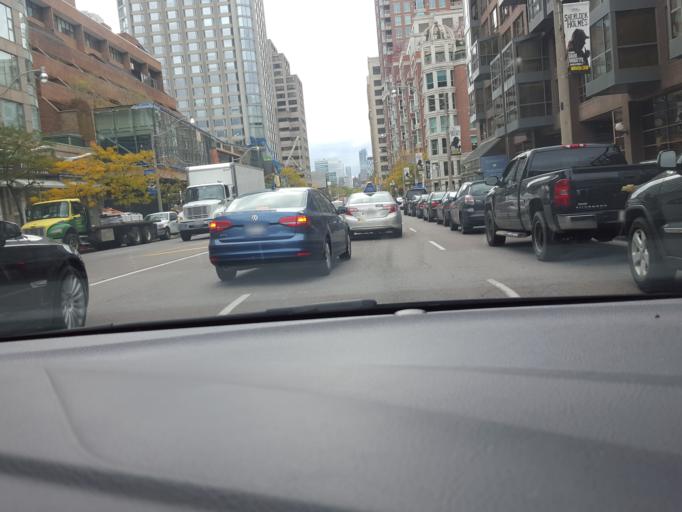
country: CA
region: Ontario
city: Toronto
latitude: 43.6717
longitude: -79.3955
